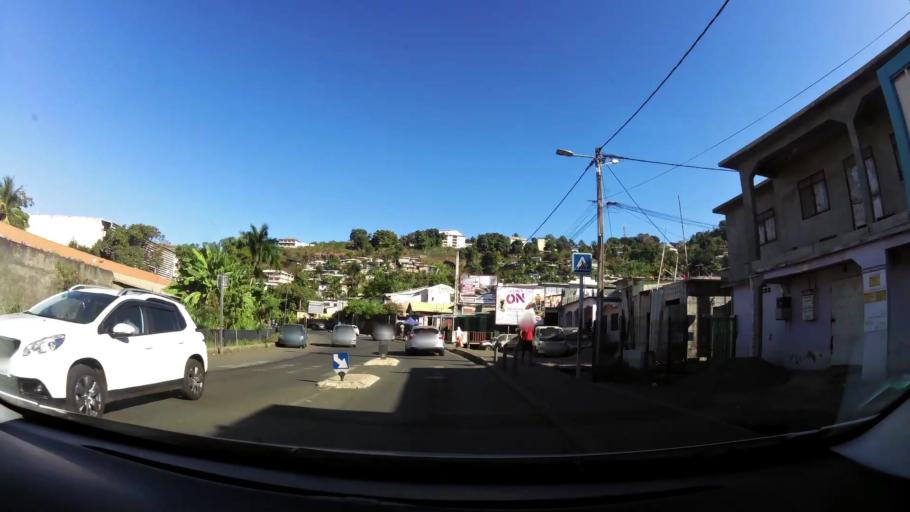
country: YT
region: Mamoudzou
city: Mamoudzou
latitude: -12.7741
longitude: 45.2228
